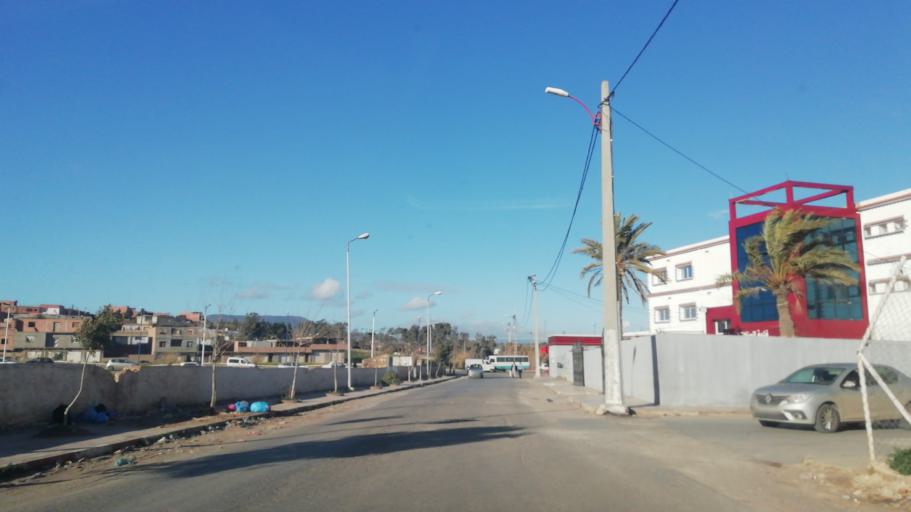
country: DZ
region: Oran
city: Sidi ech Chahmi
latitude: 35.6969
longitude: -0.4939
